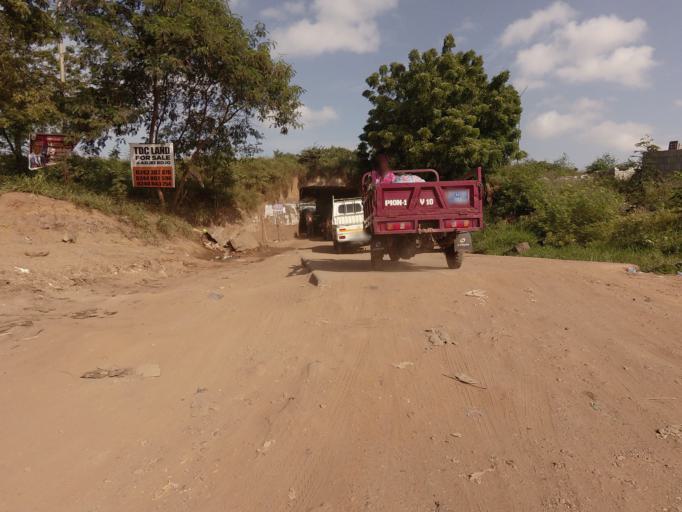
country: GH
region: Greater Accra
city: Tema
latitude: 5.6756
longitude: -0.0433
